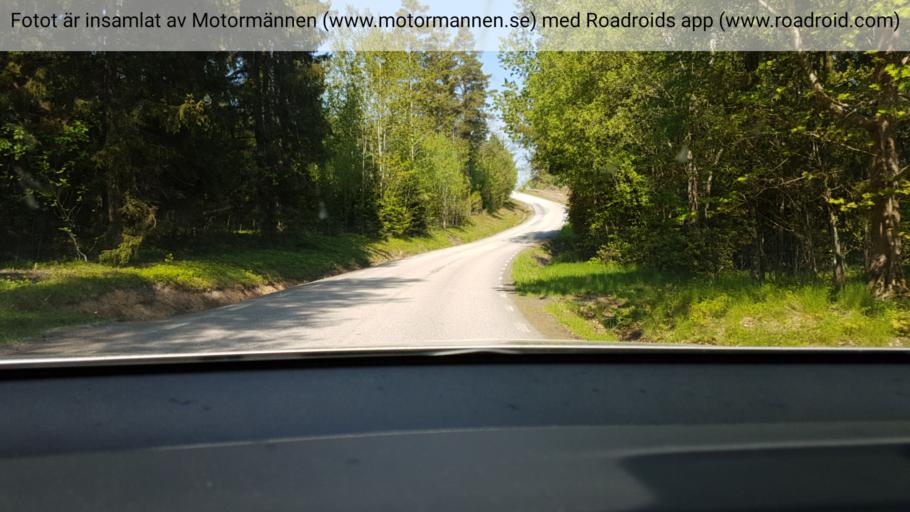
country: SE
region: Kalmar
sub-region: Vasterviks Kommun
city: Vaestervik
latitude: 57.8265
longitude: 16.5571
